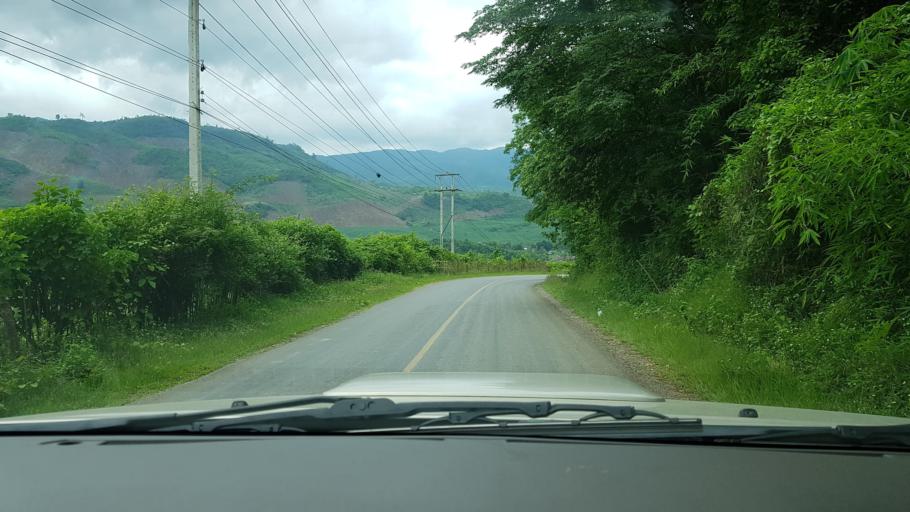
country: TH
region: Nan
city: Chaloem Phra Kiat
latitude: 19.9689
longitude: 101.2679
